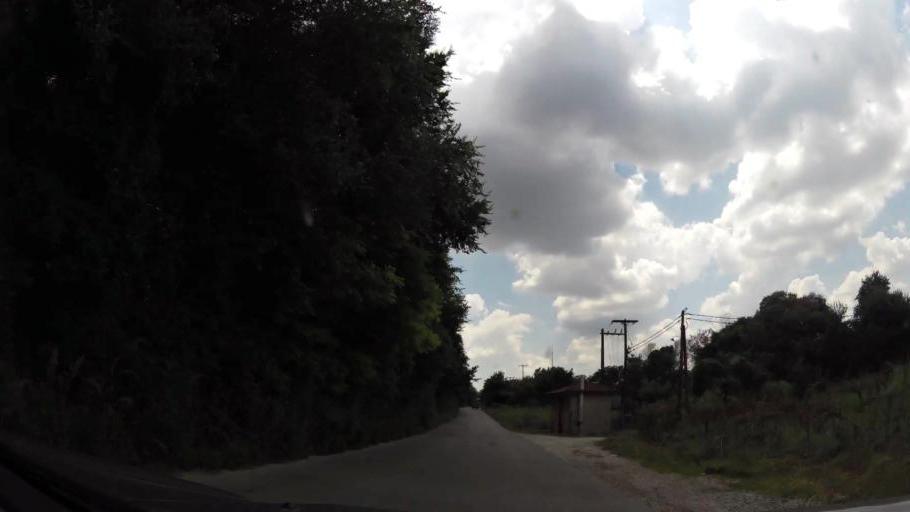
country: GR
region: West Macedonia
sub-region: Nomos Kozanis
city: Kozani
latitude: 40.2978
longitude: 21.8040
